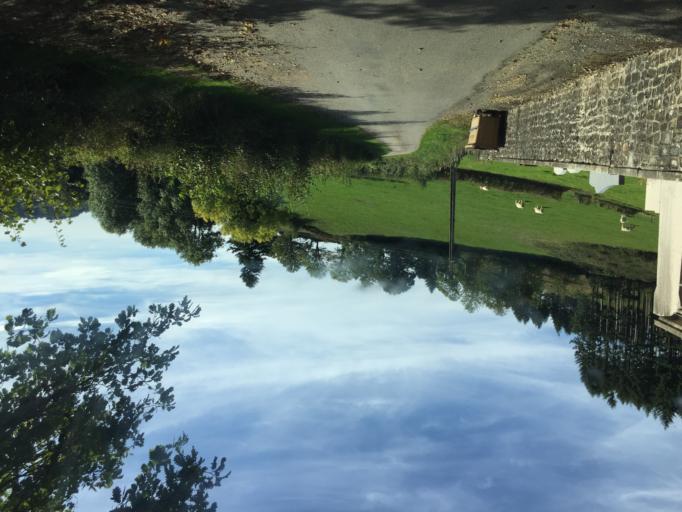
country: FR
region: Rhone-Alpes
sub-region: Departement de la Loire
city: Belmont-de-la-Loire
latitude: 46.1970
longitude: 4.4191
